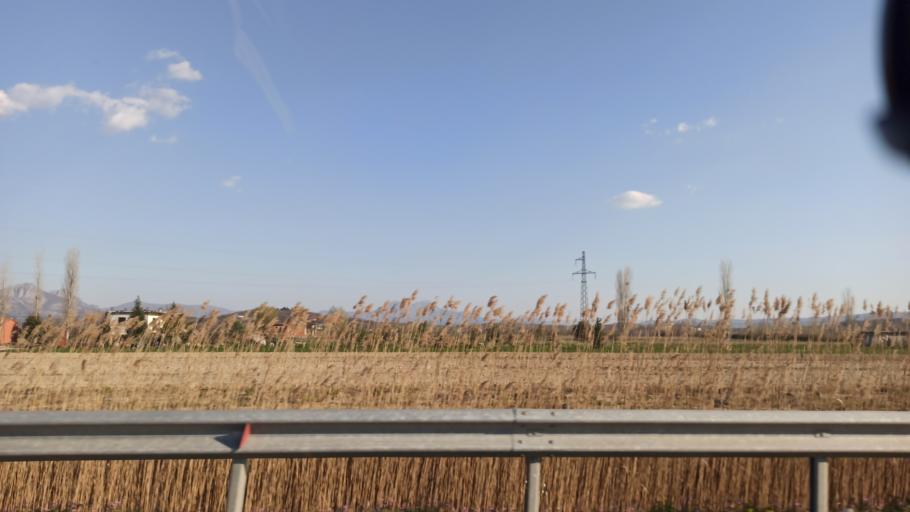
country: AL
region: Shkoder
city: Vukatane
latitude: 41.9850
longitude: 19.5456
